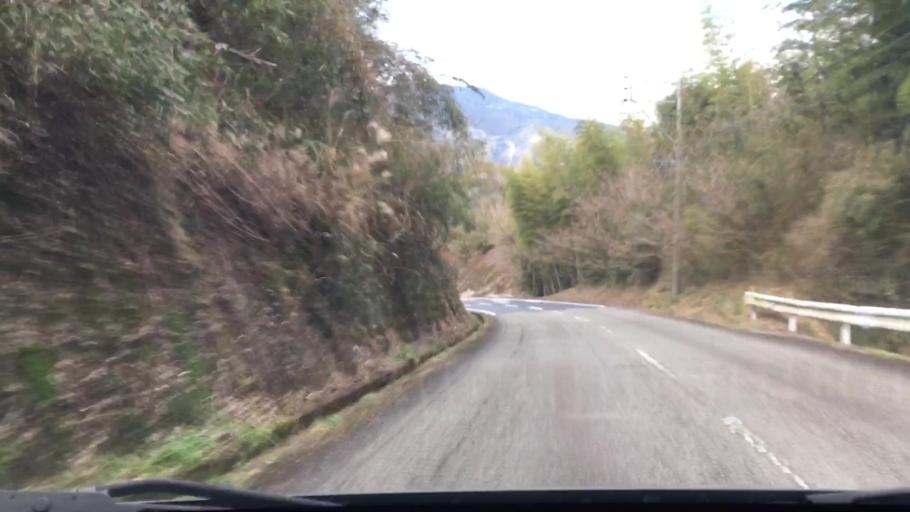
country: JP
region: Miyazaki
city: Nichinan
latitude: 31.7052
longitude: 131.3305
